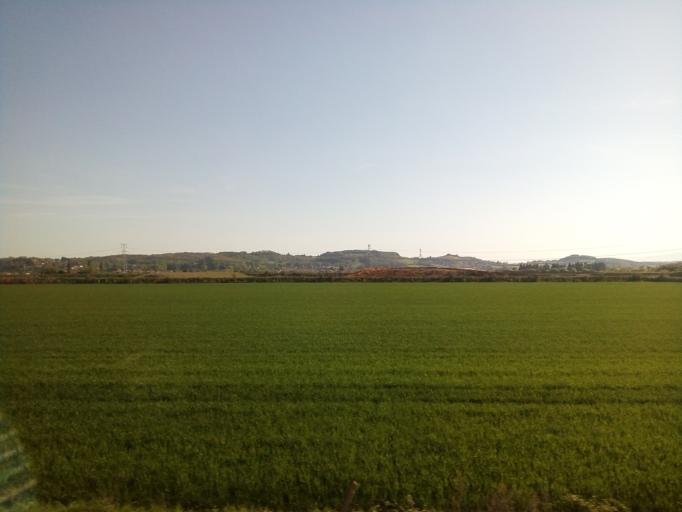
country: FR
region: Rhone-Alpes
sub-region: Departement du Rhone
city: Saint-Pierre-de-Chandieu
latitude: 45.6662
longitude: 5.0174
